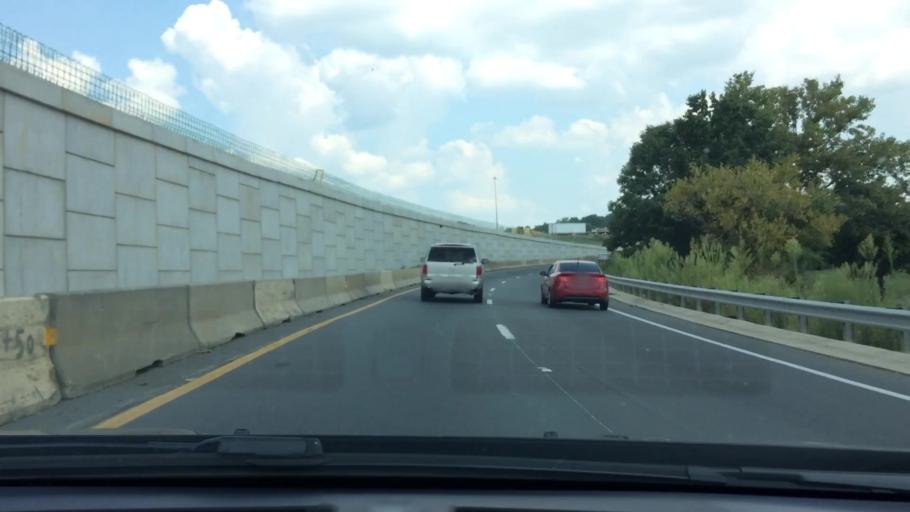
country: US
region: North Carolina
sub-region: Mecklenburg County
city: Charlotte
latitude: 35.2711
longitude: -80.8442
